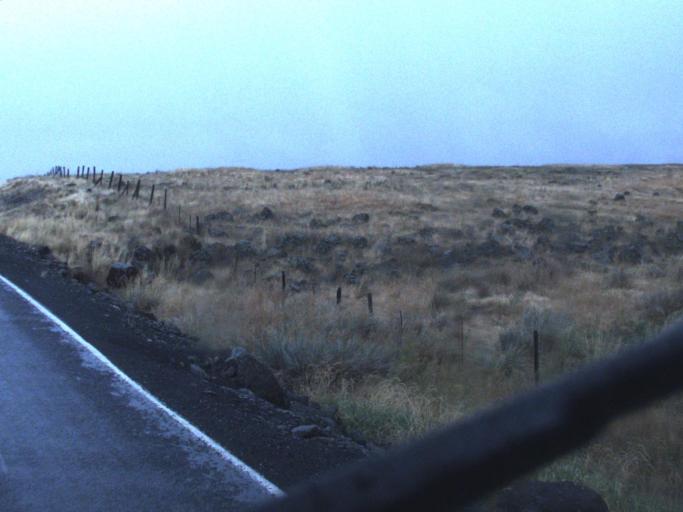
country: US
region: Washington
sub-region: Spokane County
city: Medical Lake
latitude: 47.2321
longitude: -117.9125
